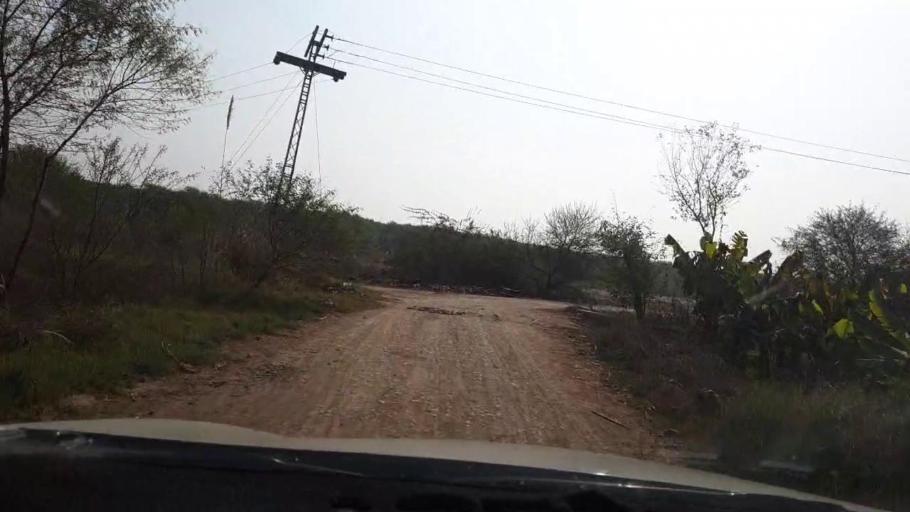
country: PK
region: Sindh
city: Matiari
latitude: 25.6231
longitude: 68.4982
